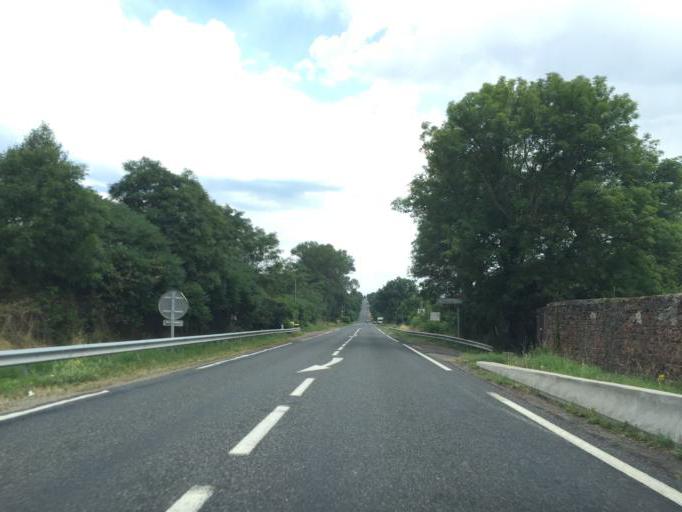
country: FR
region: Rhone-Alpes
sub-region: Departement du Rhone
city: Saint-Romain-de-Popey
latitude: 45.8652
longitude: 4.5502
